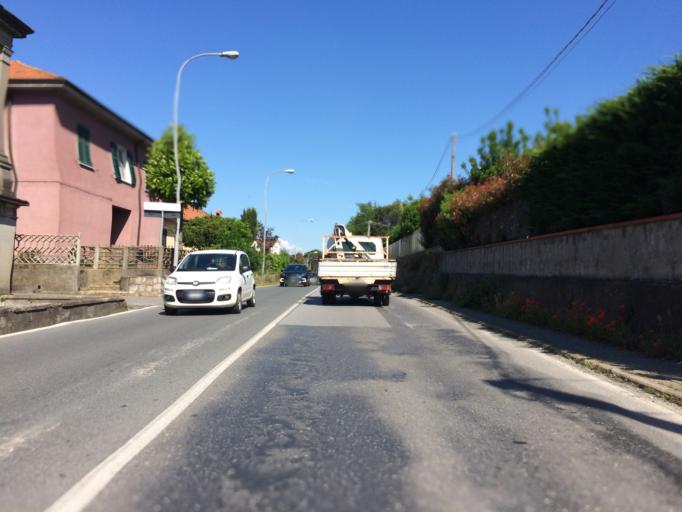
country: IT
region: Tuscany
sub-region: Provincia di Massa-Carrara
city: Borghetto-Melara
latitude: 44.1011
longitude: 9.9810
